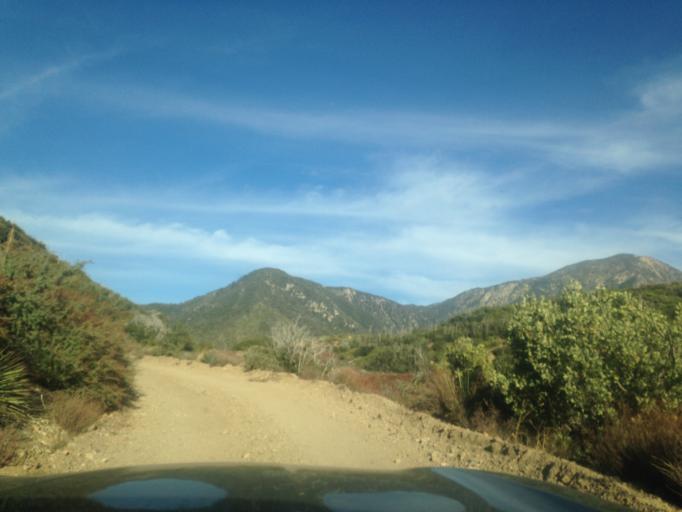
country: US
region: California
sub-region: San Bernardino County
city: Yucaipa
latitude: 34.1236
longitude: -117.0016
